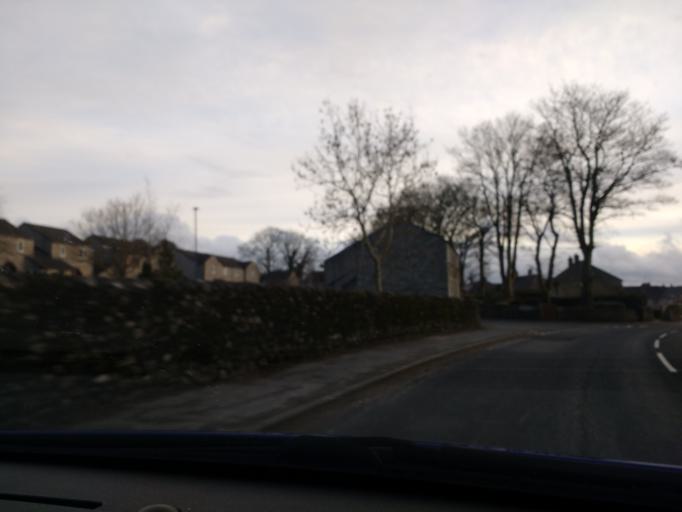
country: GB
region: England
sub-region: North Yorkshire
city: Settle
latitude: 54.0738
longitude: -2.2783
